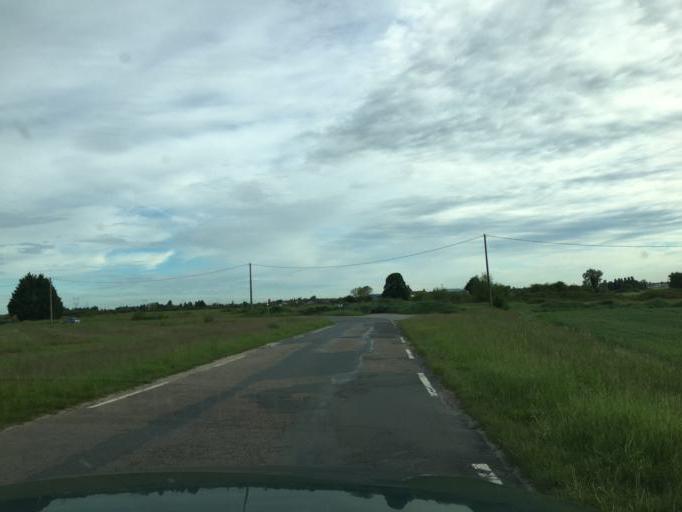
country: FR
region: Centre
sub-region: Departement du Loiret
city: Ingre
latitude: 47.9013
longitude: 1.8093
